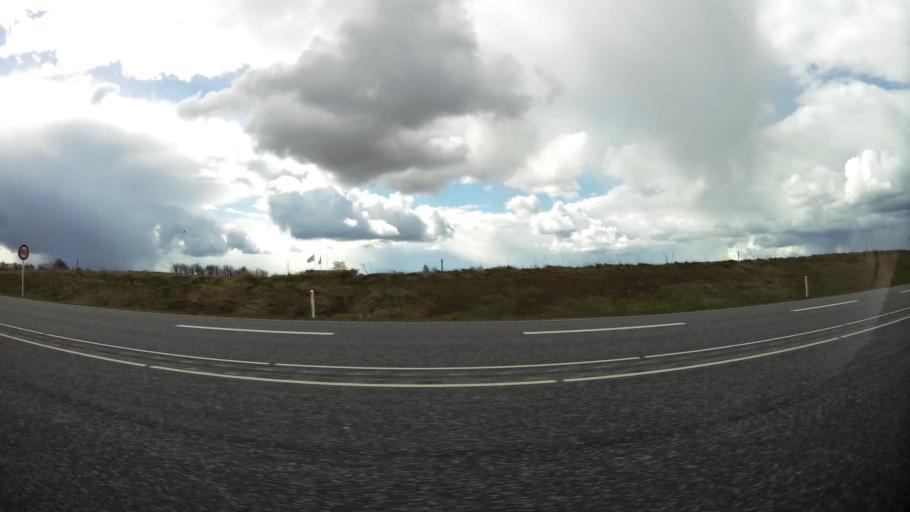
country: DK
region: South Denmark
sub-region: Vejle Kommune
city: Egtved
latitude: 55.6978
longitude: 9.3147
